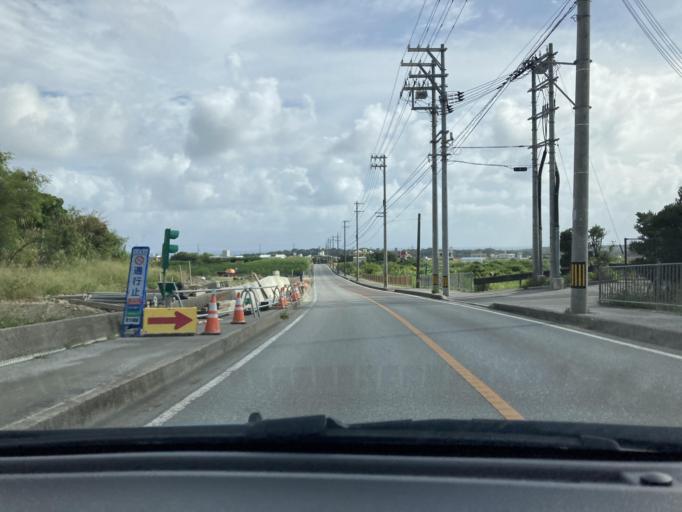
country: JP
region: Okinawa
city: Itoman
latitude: 26.1089
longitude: 127.6943
